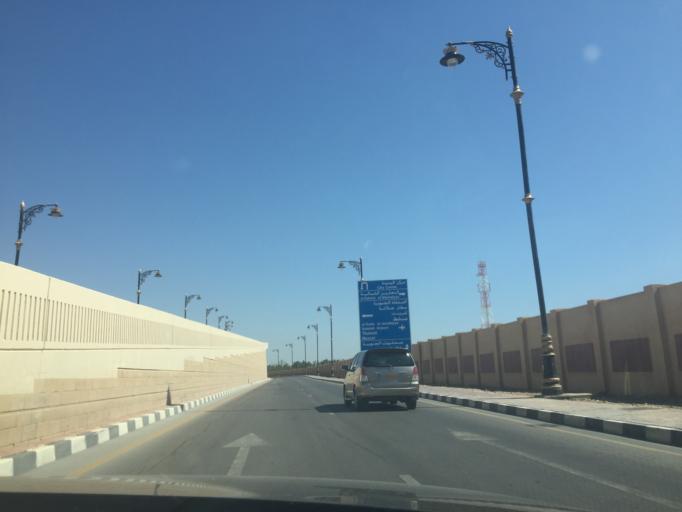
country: OM
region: Zufar
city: Salalah
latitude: 17.0303
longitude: 54.1382
